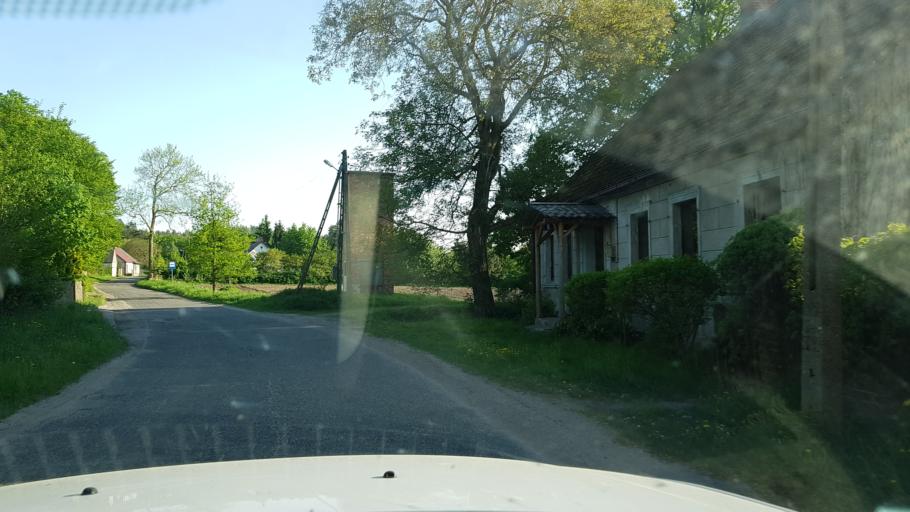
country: PL
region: West Pomeranian Voivodeship
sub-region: Powiat lobeski
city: Dobra
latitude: 53.6120
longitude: 15.3293
